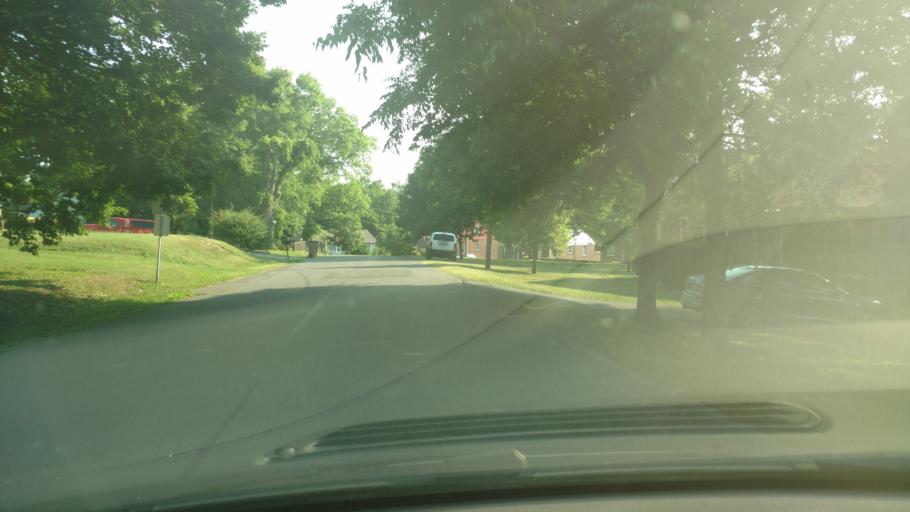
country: US
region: Tennessee
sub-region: Davidson County
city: Lakewood
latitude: 36.2136
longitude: -86.7099
